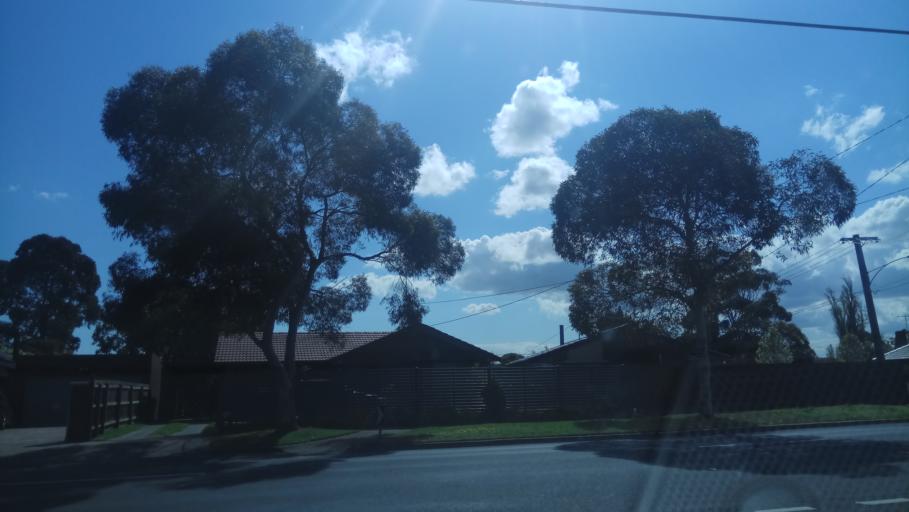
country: AU
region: Victoria
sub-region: Kingston
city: Dingley Village
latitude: -37.9872
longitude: 145.1205
